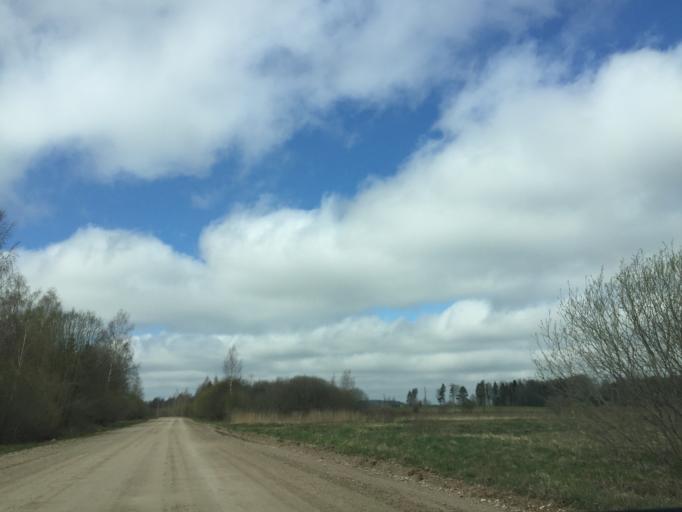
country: EE
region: Valgamaa
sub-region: Valga linn
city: Valga
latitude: 57.5408
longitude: 26.3259
